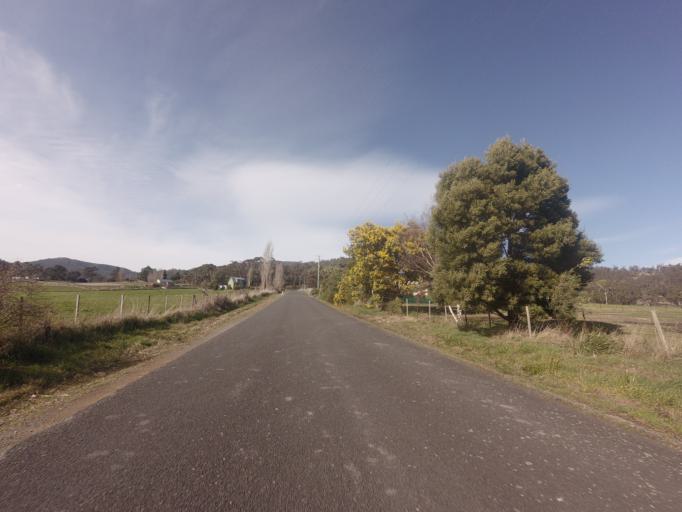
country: AU
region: Tasmania
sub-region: Huon Valley
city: Cygnet
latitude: -43.1813
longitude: 147.1200
